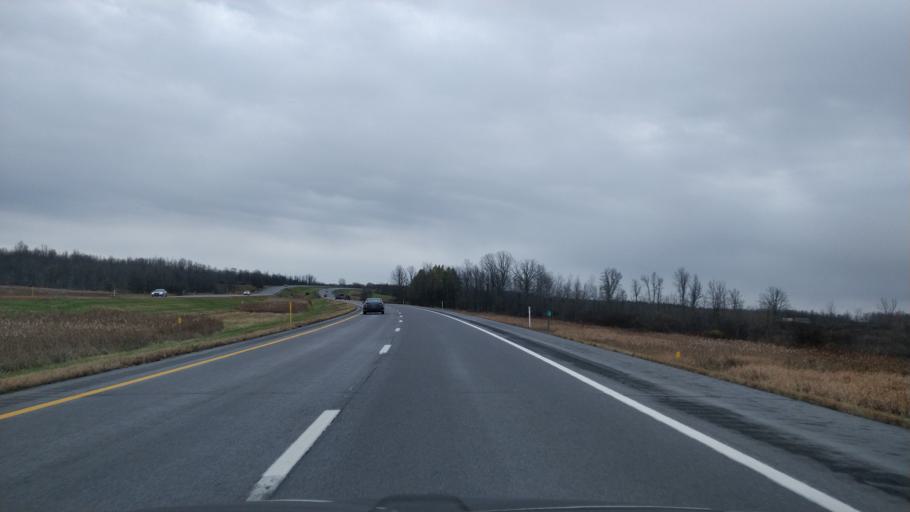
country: US
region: New York
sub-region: Jefferson County
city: Calcium
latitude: 44.1462
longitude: -75.8855
